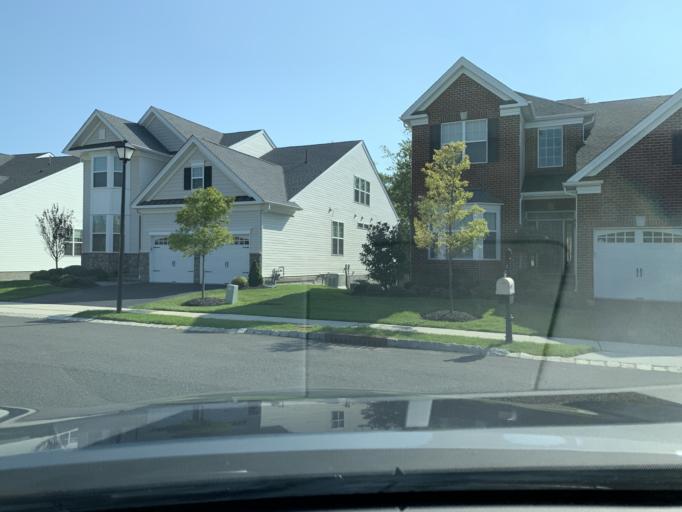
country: US
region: New Jersey
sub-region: Monmouth County
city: Shrewsbury
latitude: 40.3139
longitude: -74.0572
